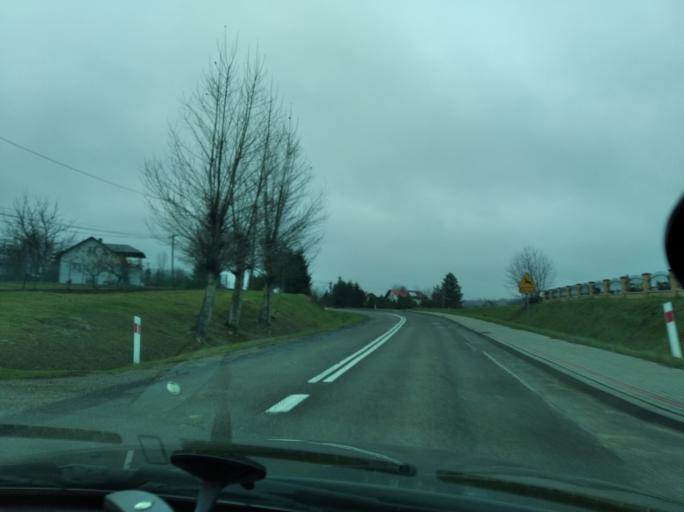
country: PL
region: Subcarpathian Voivodeship
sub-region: Powiat przeworski
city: Jawornik Polski
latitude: 49.8706
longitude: 22.2458
